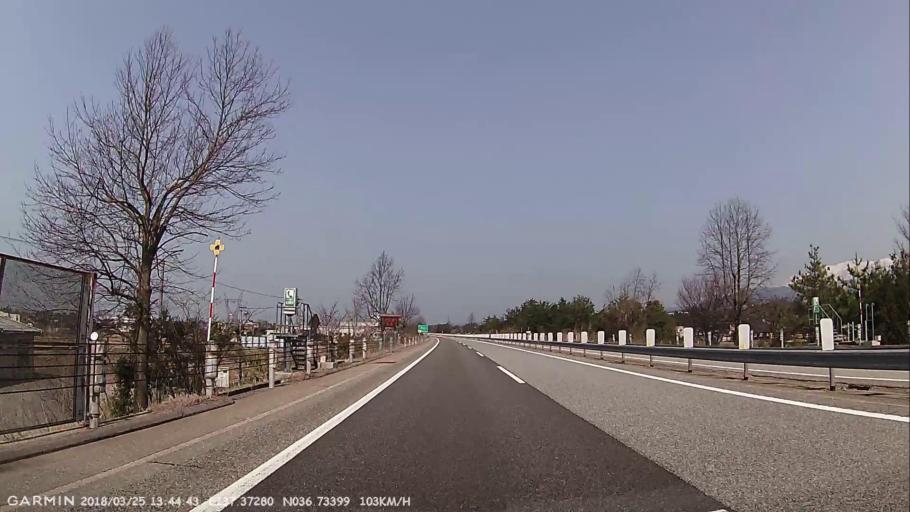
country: JP
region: Toyama
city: Kamiichi
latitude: 36.7342
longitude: 137.3730
